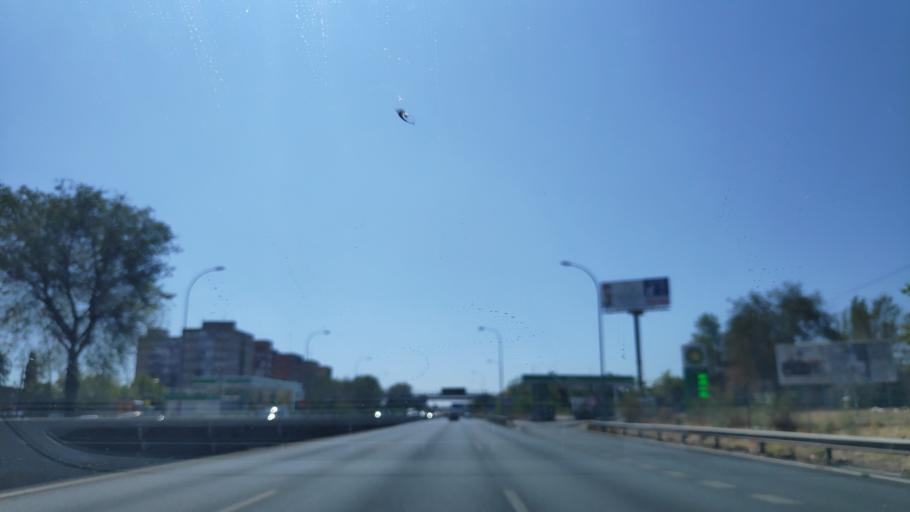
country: ES
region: Madrid
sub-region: Provincia de Madrid
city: Getafe
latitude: 40.3040
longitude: -3.7393
